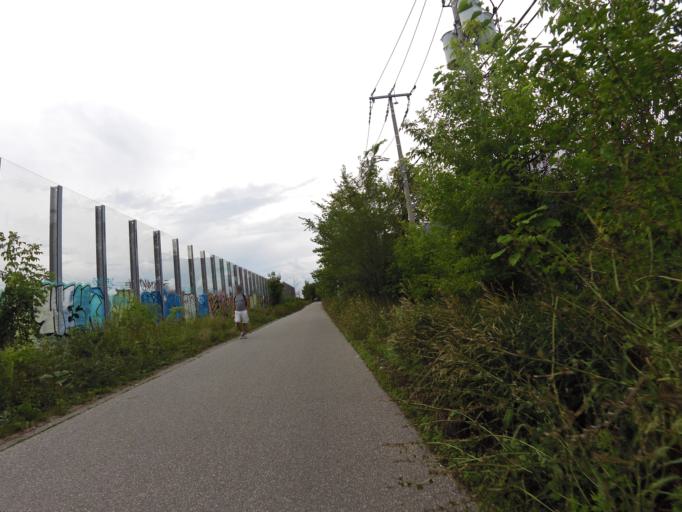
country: CA
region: Ontario
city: Toronto
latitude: 43.6625
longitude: -79.4551
